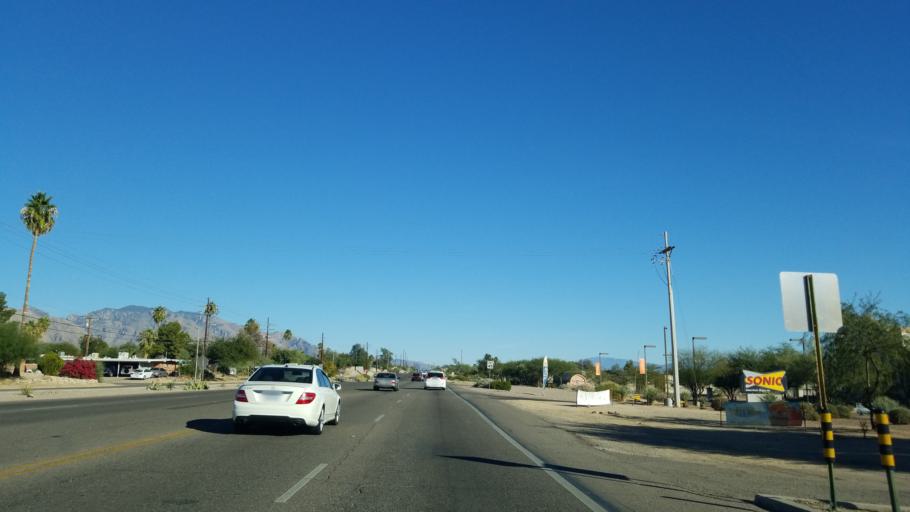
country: US
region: Arizona
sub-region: Pima County
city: Flowing Wells
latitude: 32.3232
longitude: -111.0368
